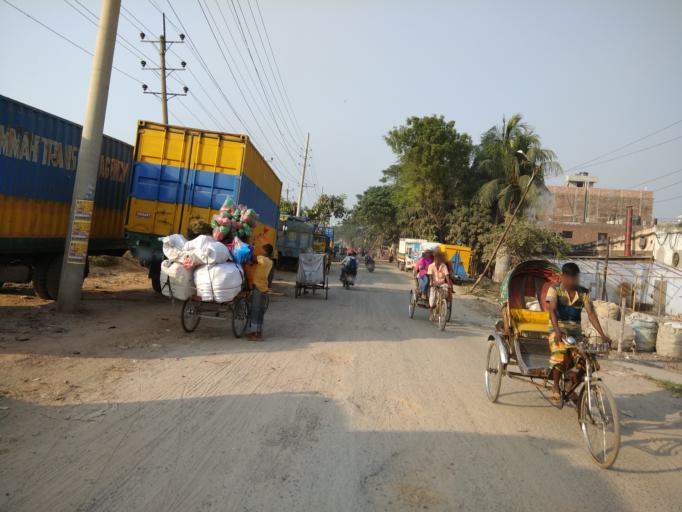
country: BD
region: Dhaka
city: Azimpur
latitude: 23.7168
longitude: 90.3794
